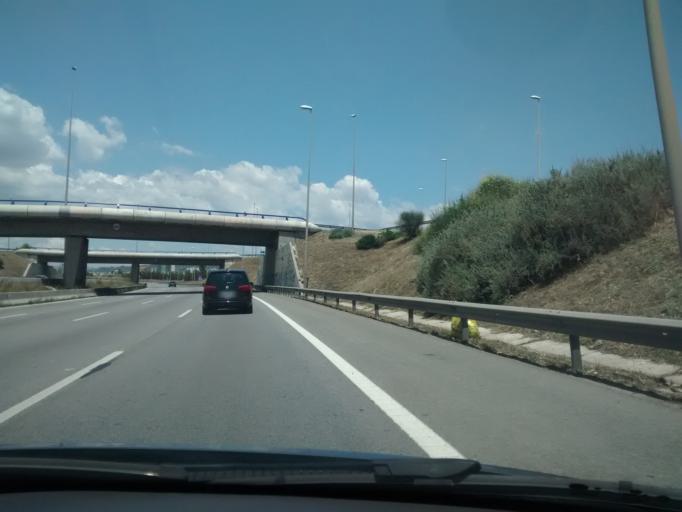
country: ES
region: Catalonia
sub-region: Provincia de Barcelona
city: Sant Joan Despi
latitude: 41.3620
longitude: 2.0510
